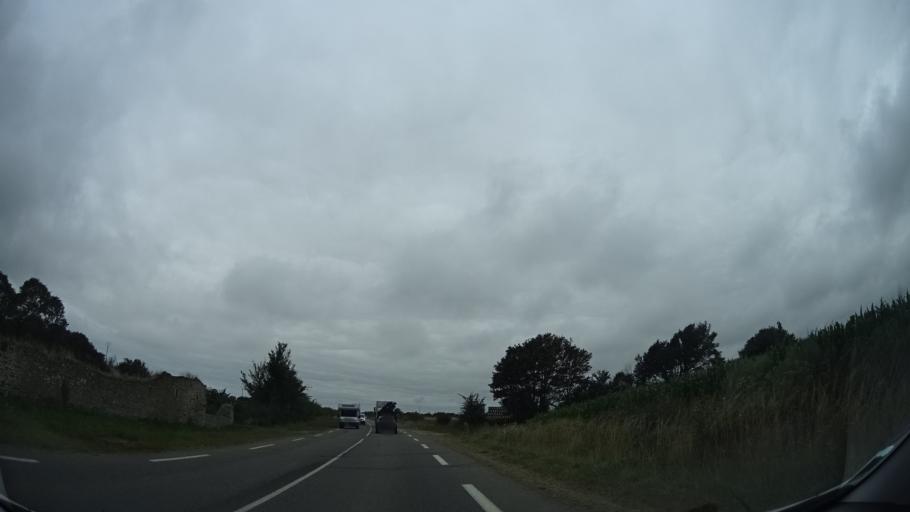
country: FR
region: Lower Normandy
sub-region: Departement de la Manche
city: Portbail
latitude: 49.3606
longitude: -1.6904
